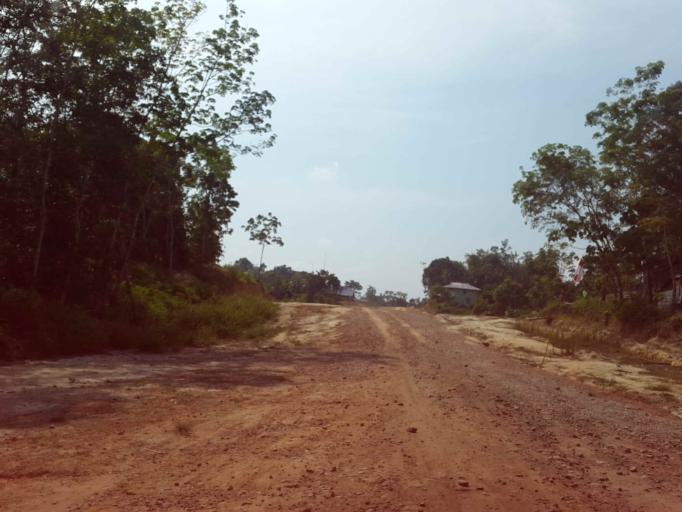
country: MY
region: Sarawak
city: Simanggang
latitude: 0.7782
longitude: 111.6223
